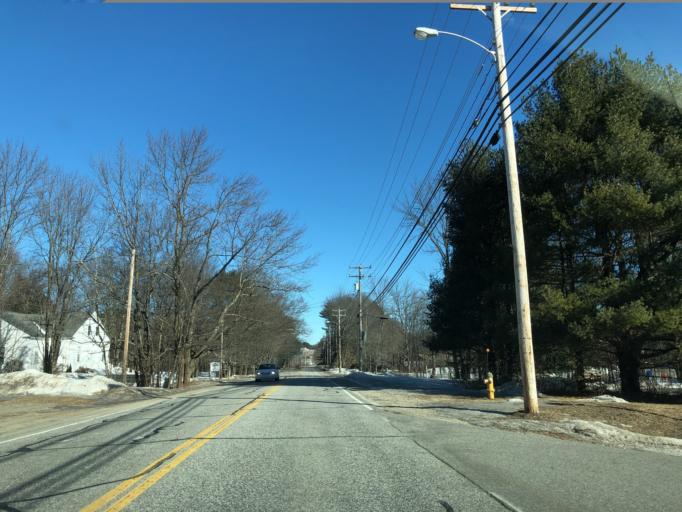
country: US
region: Maine
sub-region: Cumberland County
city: South Windham
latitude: 43.7795
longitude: -70.4157
